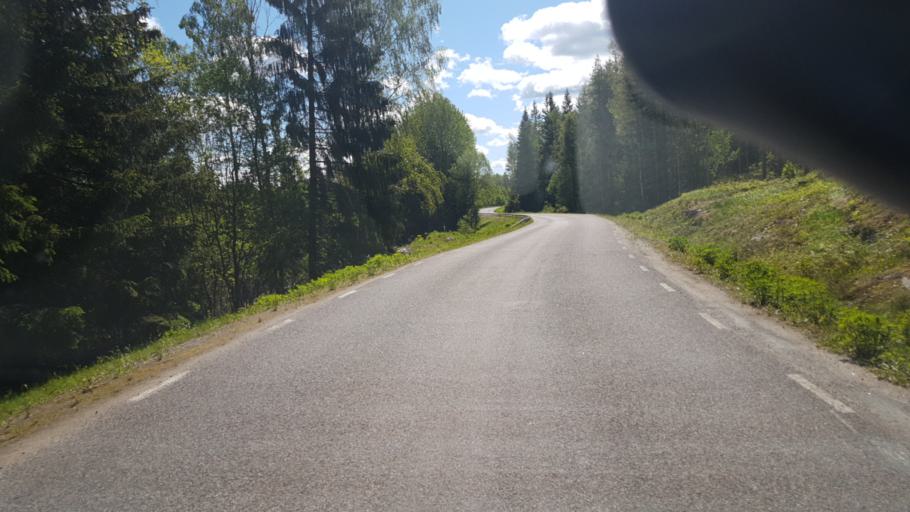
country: SE
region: Vaermland
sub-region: Grums Kommun
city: Grums
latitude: 59.5139
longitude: 12.8585
